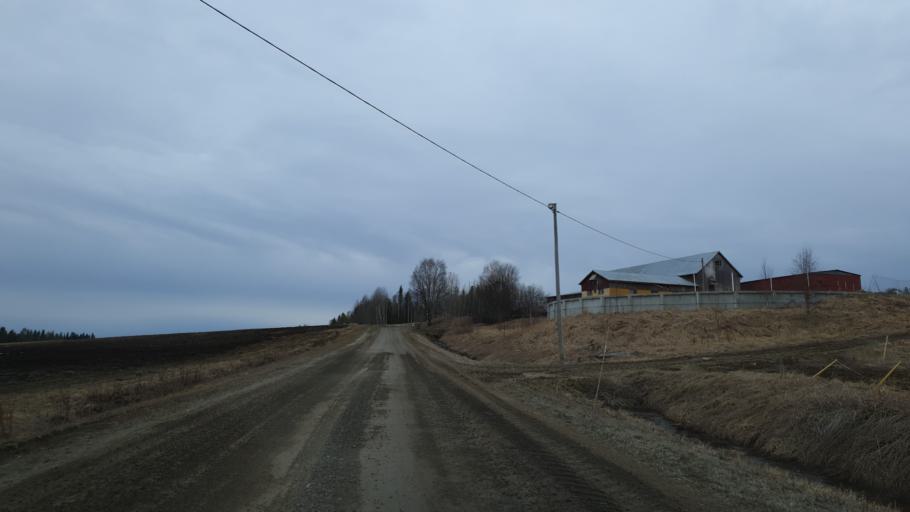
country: SE
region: Vaesterbotten
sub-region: Skelleftea Kommun
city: Burea
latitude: 64.3404
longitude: 21.1265
